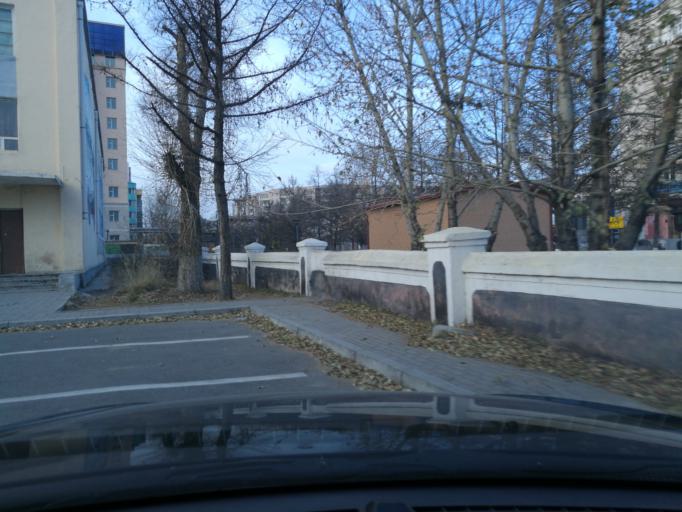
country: MN
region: Ulaanbaatar
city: Ulaanbaatar
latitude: 47.9241
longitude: 106.9272
